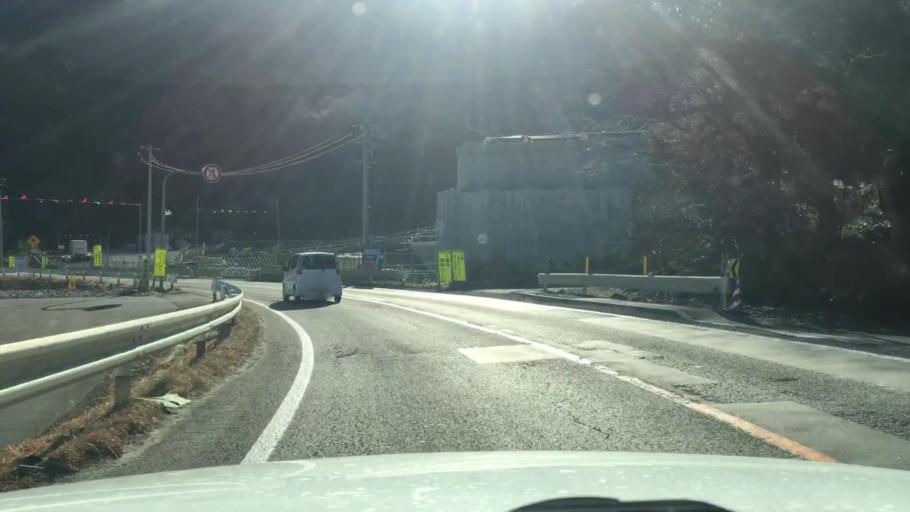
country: JP
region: Iwate
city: Miyako
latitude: 39.5998
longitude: 141.7610
